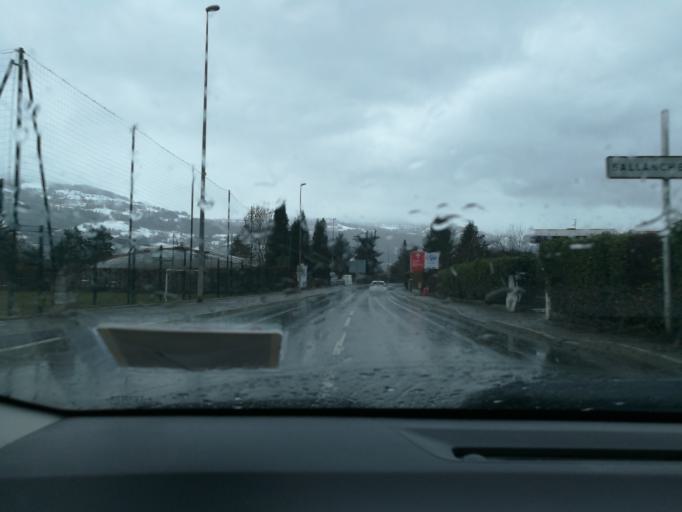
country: FR
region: Rhone-Alpes
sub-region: Departement de la Haute-Savoie
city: Passy
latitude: 45.9171
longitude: 6.6981
